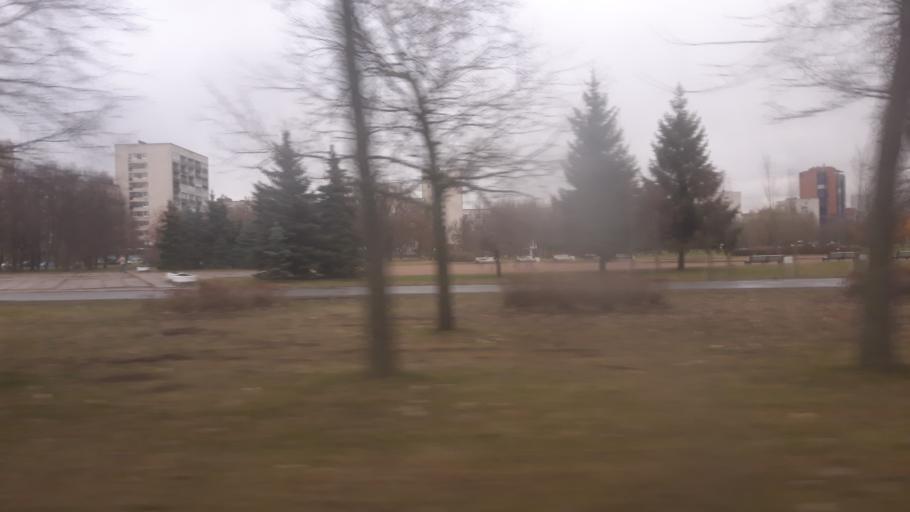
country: RU
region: St.-Petersburg
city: Kupchino
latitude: 59.8404
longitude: 30.3224
